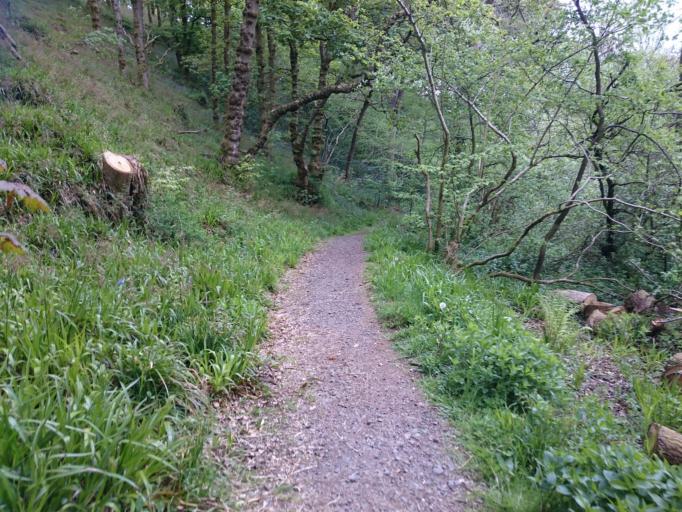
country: GB
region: Scotland
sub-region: Falkirk
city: Dunipace
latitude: 56.0274
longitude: -3.9483
